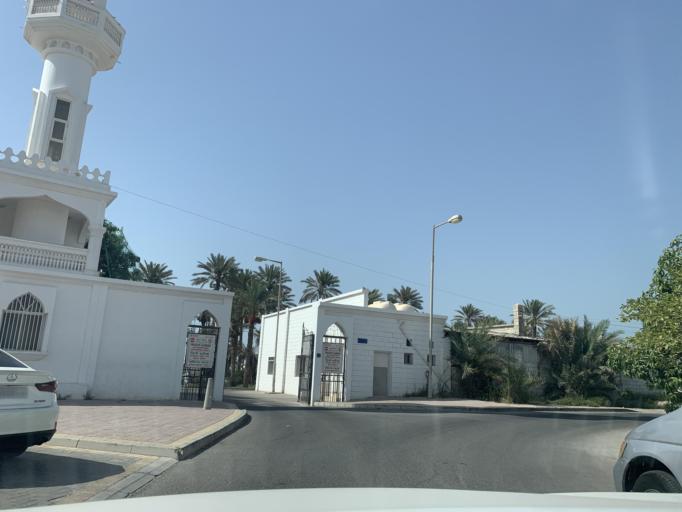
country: BH
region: Manama
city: Jidd Hafs
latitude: 26.2309
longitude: 50.4757
